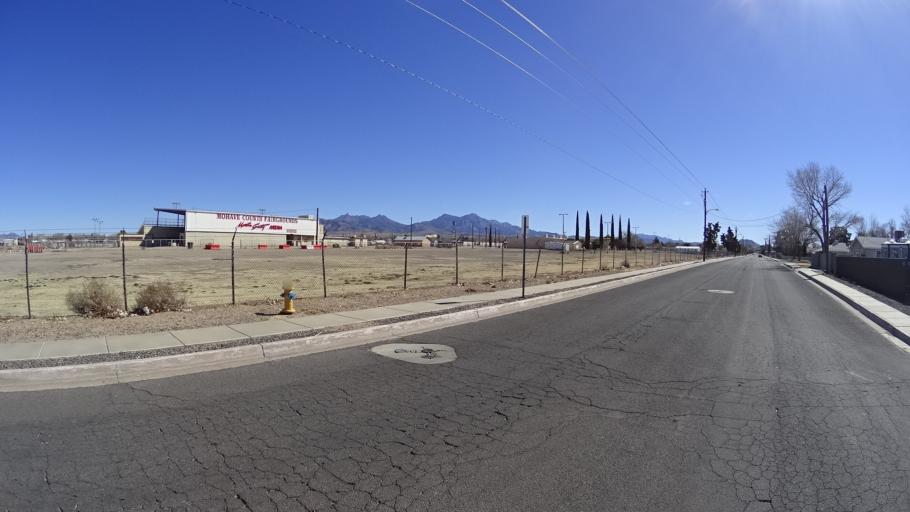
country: US
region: Arizona
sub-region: Mohave County
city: Kingman
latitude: 35.2133
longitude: -114.0291
